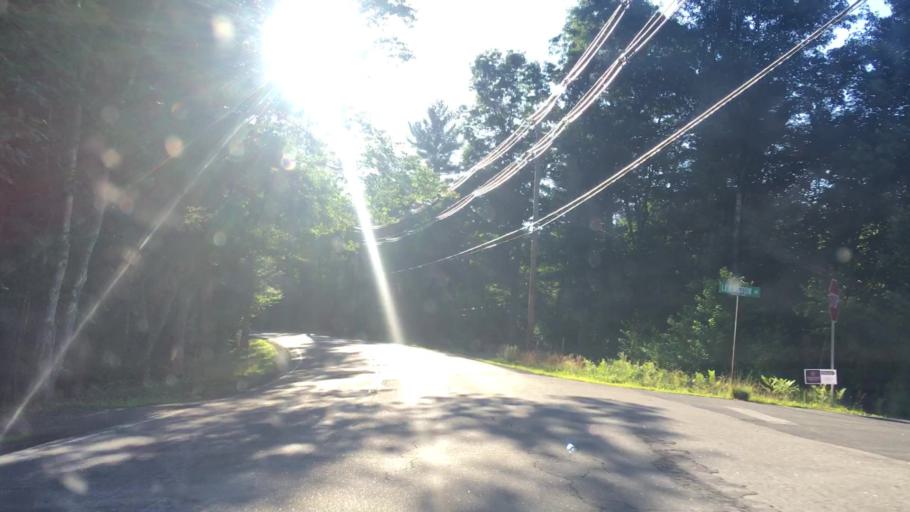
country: US
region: New Hampshire
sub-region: Rockingham County
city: Chester
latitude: 42.9563
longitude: -71.2189
